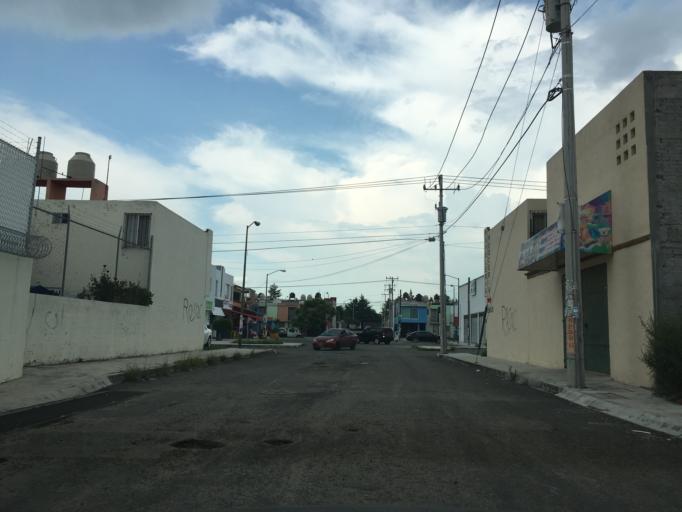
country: MX
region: Michoacan
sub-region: Morelia
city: Morelos
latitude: 19.6715
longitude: -101.2408
